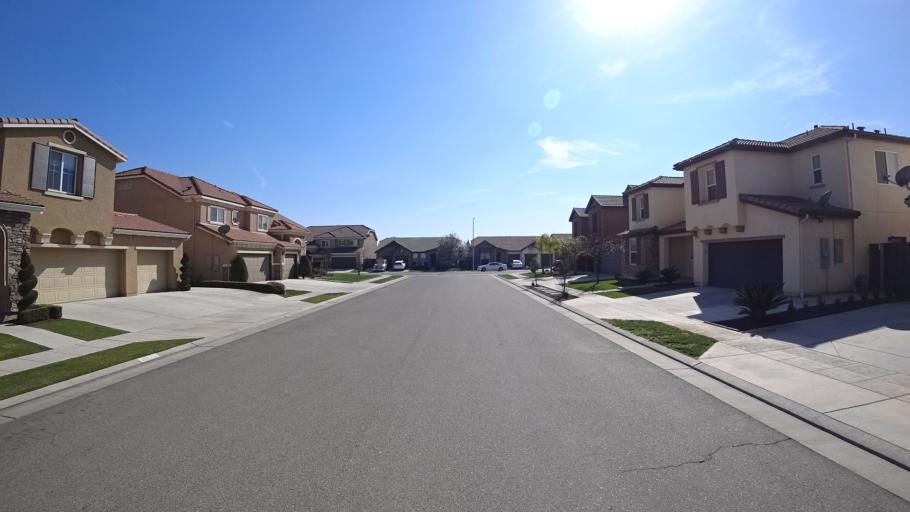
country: US
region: California
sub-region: Fresno County
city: Clovis
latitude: 36.8908
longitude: -119.7403
